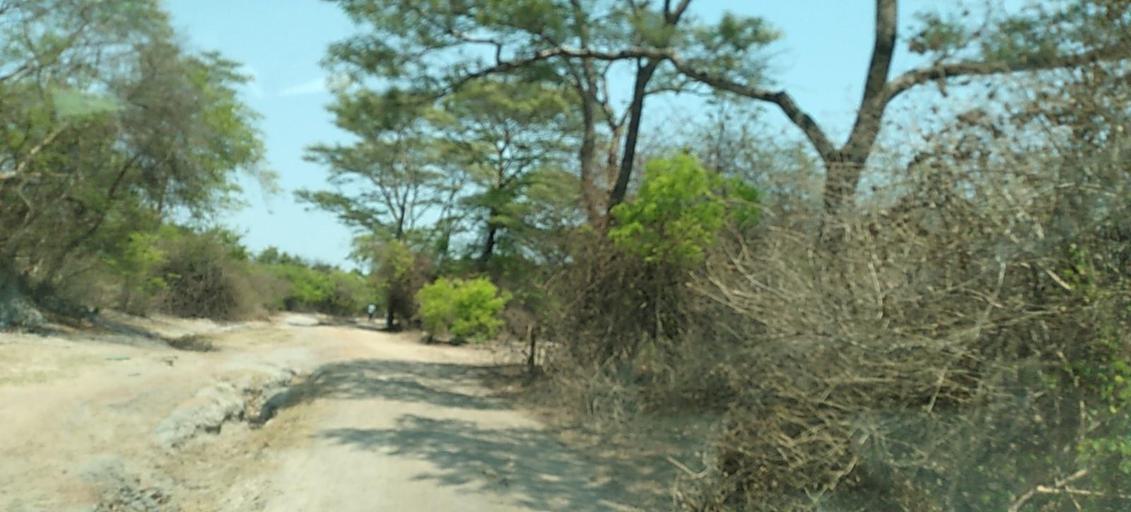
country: ZM
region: Copperbelt
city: Mpongwe
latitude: -13.8671
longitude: 27.8824
